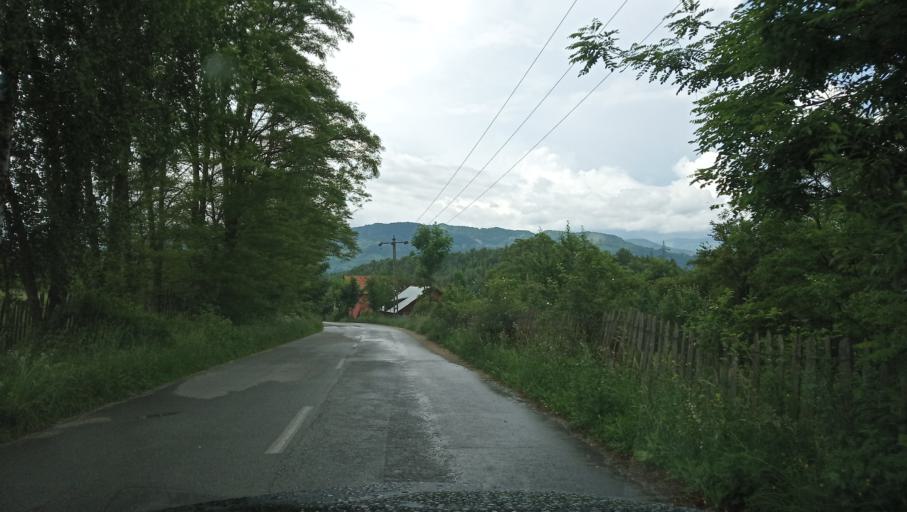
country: RO
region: Hunedoara
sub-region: Oras Petrila
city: Petrila
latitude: 45.4162
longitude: 23.4112
